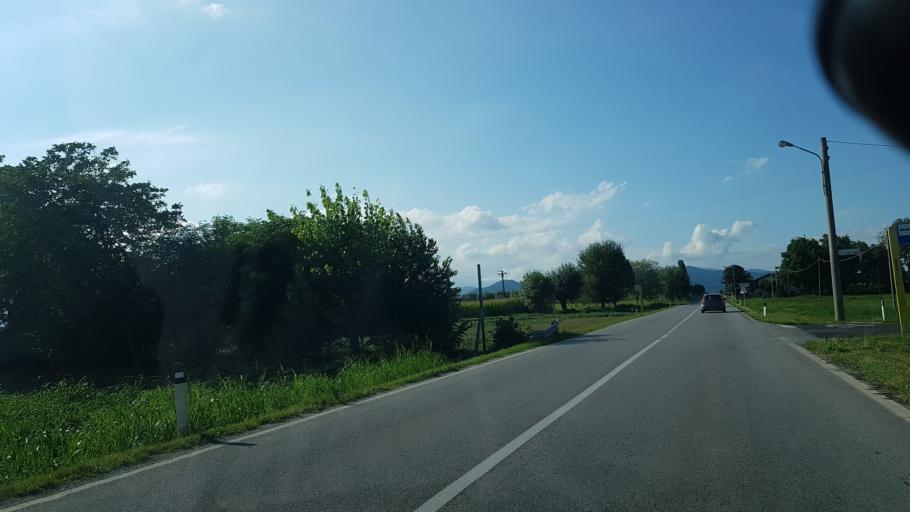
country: IT
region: Piedmont
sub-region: Provincia di Cuneo
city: Roata Rossi
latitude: 44.4627
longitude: 7.5172
